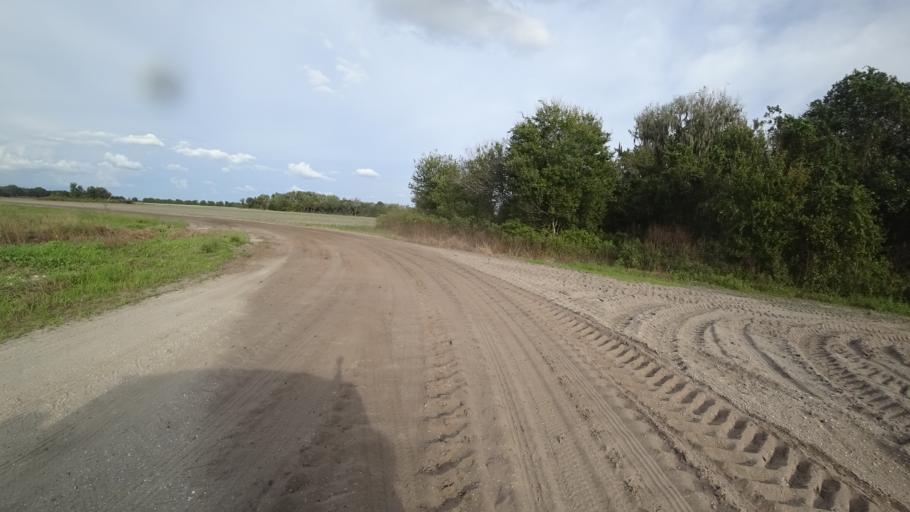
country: US
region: Florida
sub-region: Hardee County
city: Bowling Green
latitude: 27.5665
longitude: -82.0757
